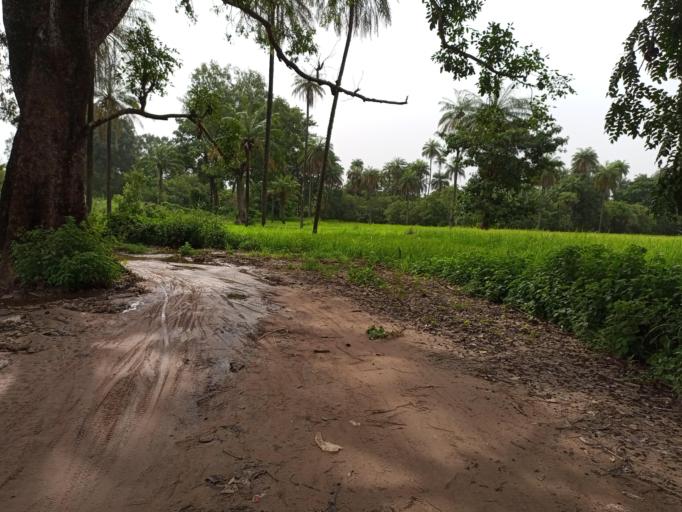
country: GW
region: Oio
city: Farim
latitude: 12.4308
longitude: -15.4144
